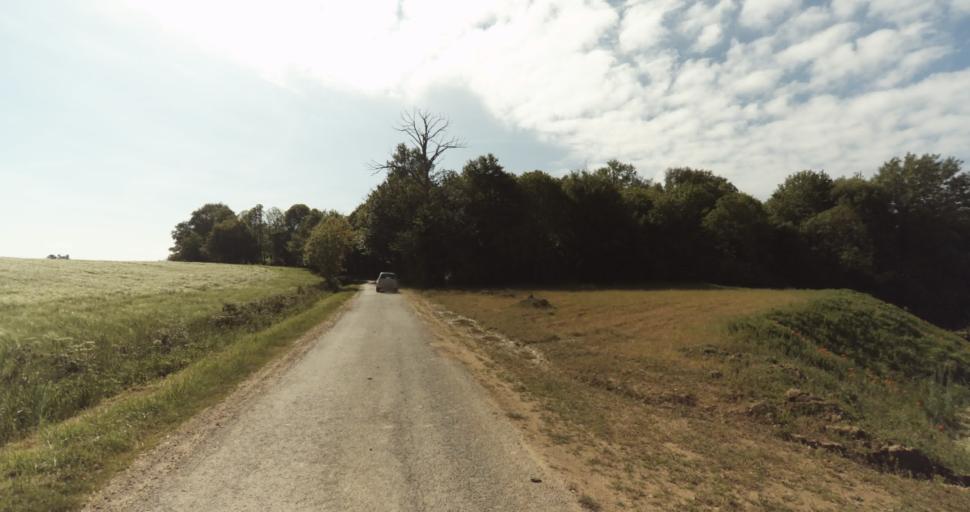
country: FR
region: Limousin
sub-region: Departement de la Haute-Vienne
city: Solignac
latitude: 45.7205
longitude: 1.2607
